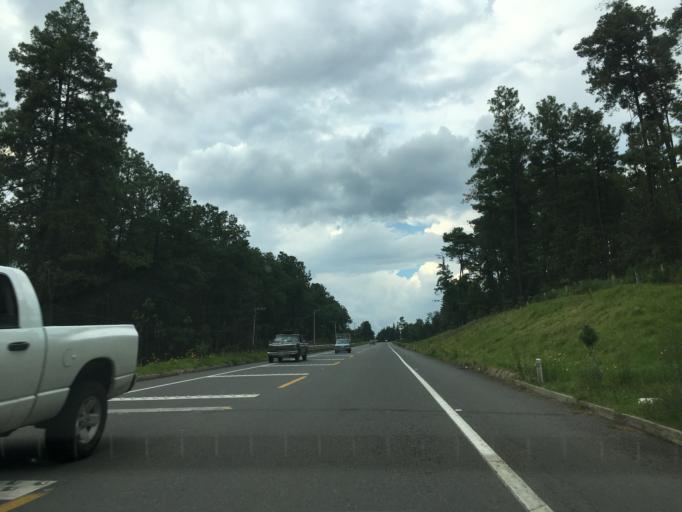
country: MX
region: Michoacan
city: Angahuan
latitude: 19.5200
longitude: -102.1796
